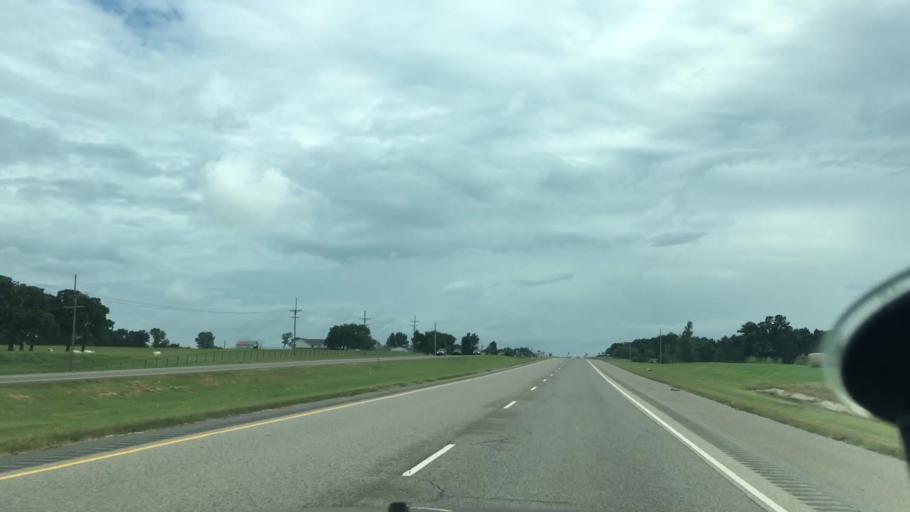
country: US
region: Oklahoma
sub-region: Lincoln County
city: Prague
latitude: 35.3583
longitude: -96.6718
